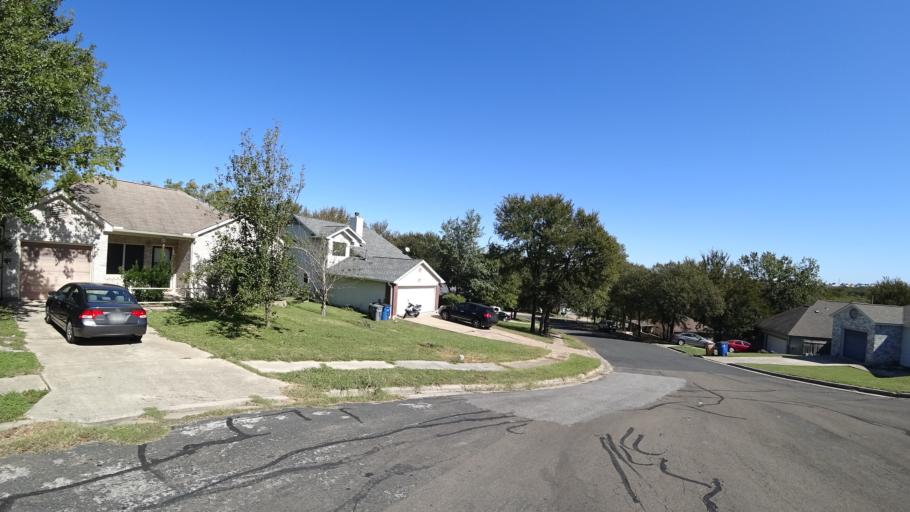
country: US
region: Texas
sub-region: Travis County
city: Austin
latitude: 30.2903
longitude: -97.6599
